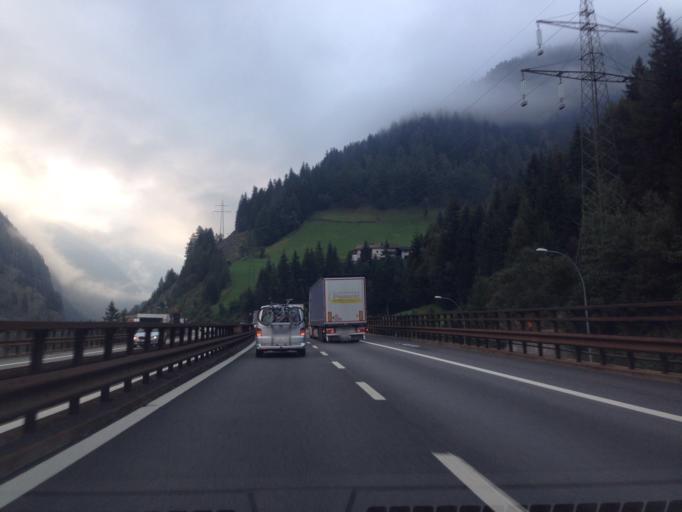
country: IT
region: Trentino-Alto Adige
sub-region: Bolzano
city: Colle Isarco
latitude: 46.9524
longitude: 11.4562
